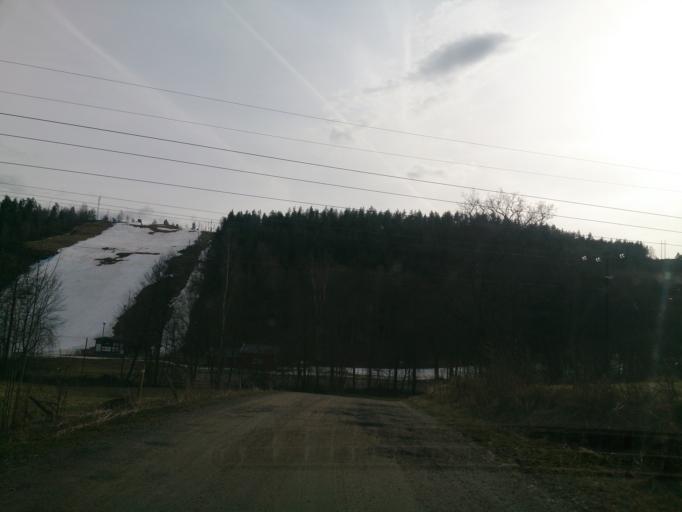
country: SE
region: OEstergoetland
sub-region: Norrkopings Kommun
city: Jursla
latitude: 58.6720
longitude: 16.1367
